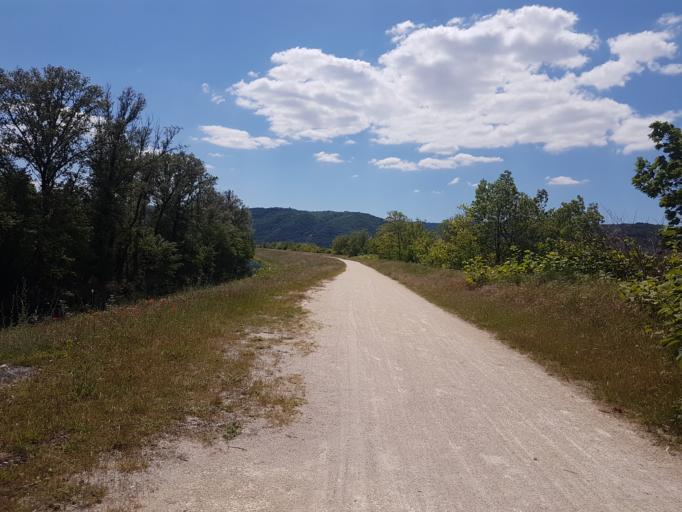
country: FR
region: Rhone-Alpes
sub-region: Departement de l'Ardeche
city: Mauves
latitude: 45.0415
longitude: 4.8486
